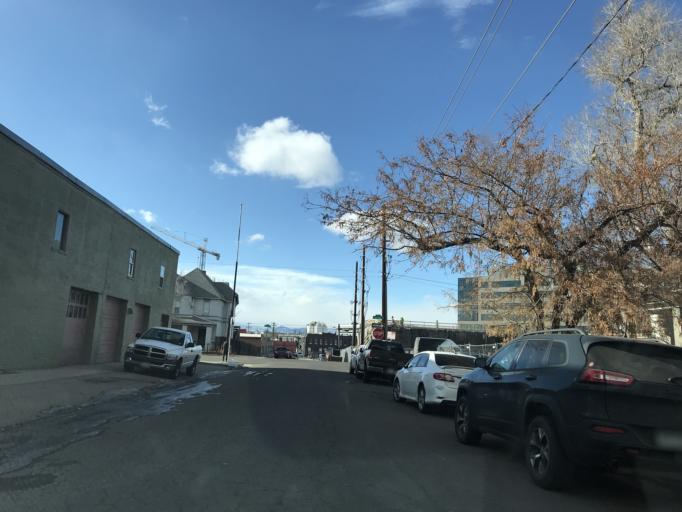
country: US
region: Colorado
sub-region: Denver County
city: Denver
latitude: 39.7682
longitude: -104.9712
